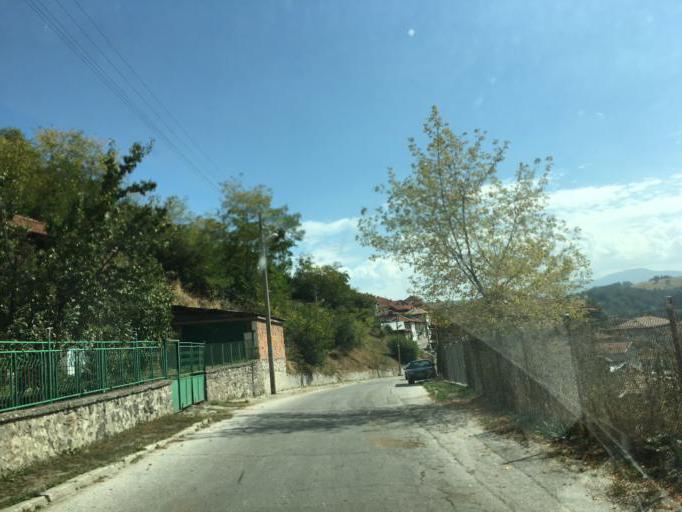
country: BG
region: Pazardzhik
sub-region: Obshtina Bratsigovo
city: Bratsigovo
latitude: 41.8854
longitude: 24.3467
